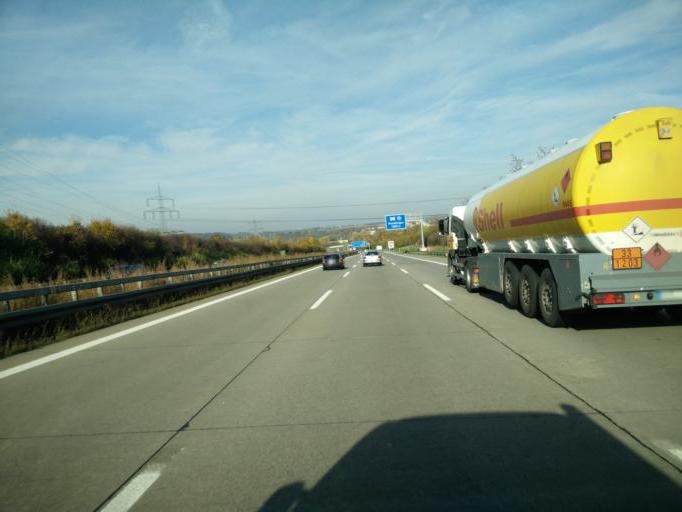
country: DE
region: Baden-Wuerttemberg
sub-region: Regierungsbezirk Stuttgart
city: Wendlingen am Neckar
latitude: 48.6603
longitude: 9.3771
